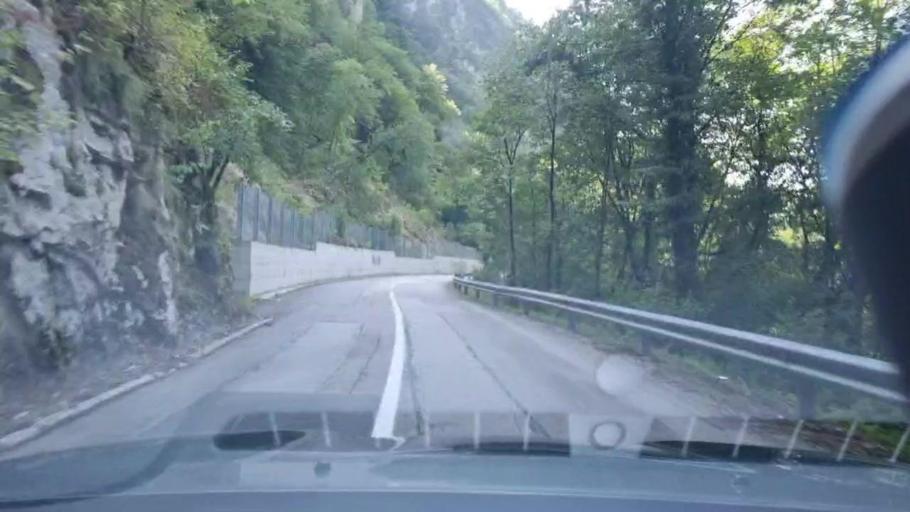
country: BA
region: Federation of Bosnia and Herzegovina
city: Stijena
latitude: 44.8809
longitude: 16.0693
